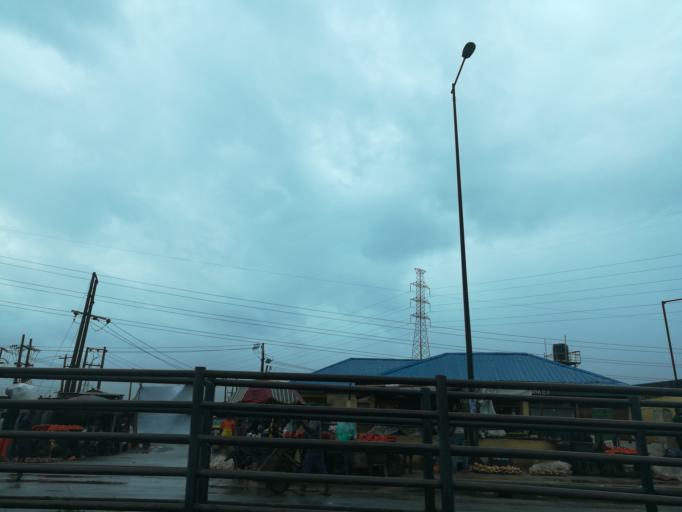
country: NG
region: Lagos
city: Ojota
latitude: 6.6053
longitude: 3.4006
